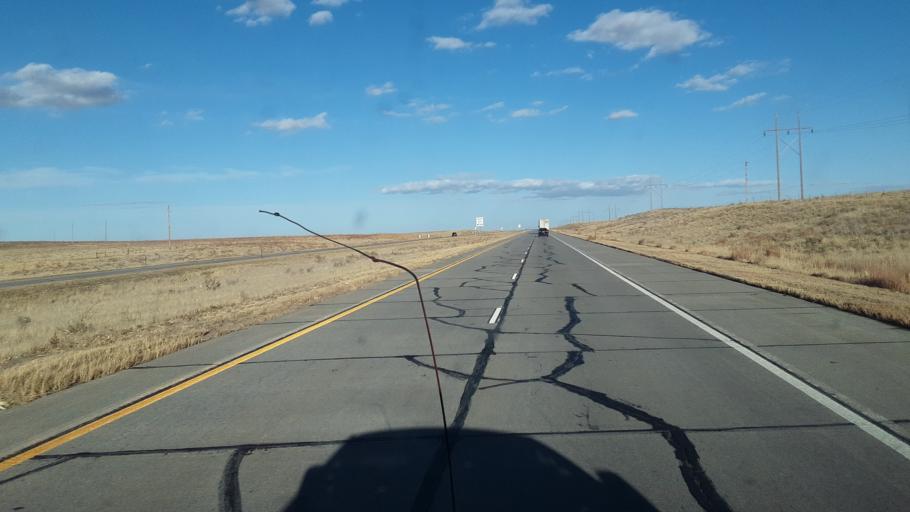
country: US
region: Nebraska
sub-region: Cheyenne County
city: Sidney
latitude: 40.7961
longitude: -102.8777
